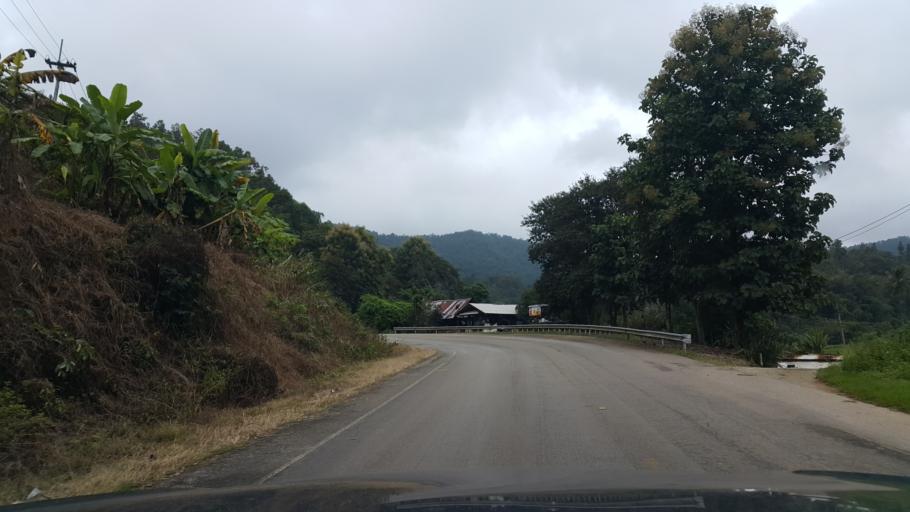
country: TH
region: Chiang Mai
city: Samoeng
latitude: 18.8085
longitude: 98.8241
